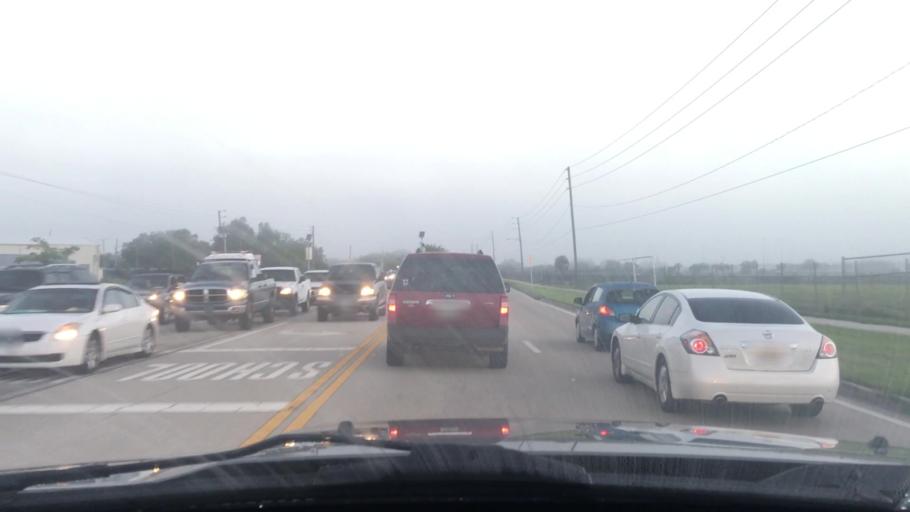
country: US
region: Florida
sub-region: Highlands County
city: Sebring
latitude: 27.4905
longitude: -81.4334
